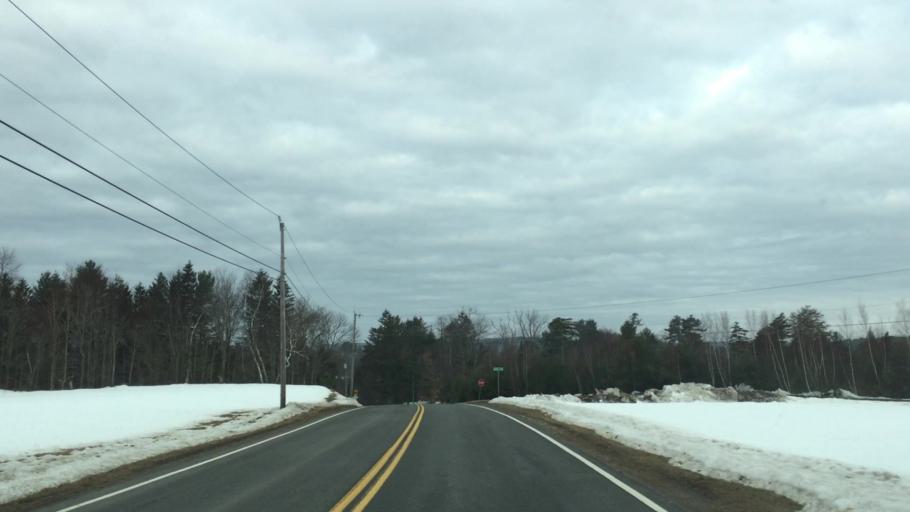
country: US
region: Massachusetts
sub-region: Berkshire County
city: Hinsdale
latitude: 42.4224
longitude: -73.0782
